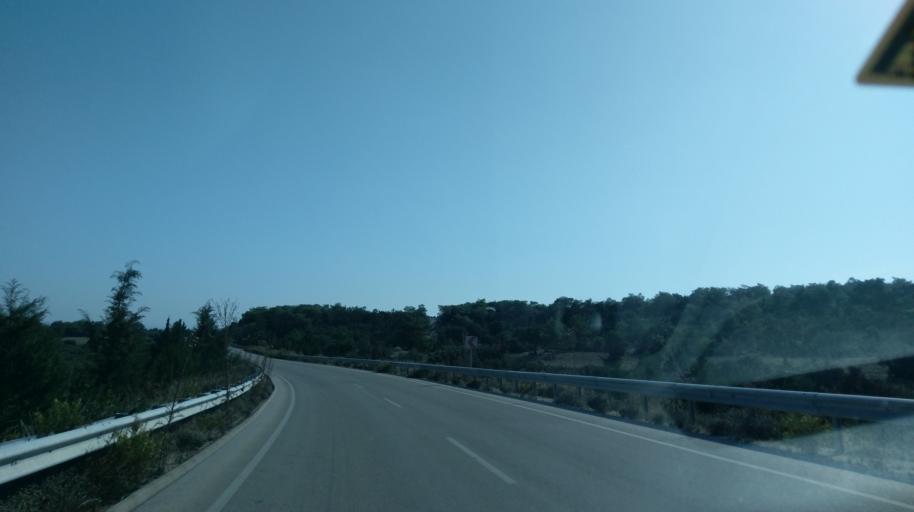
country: CY
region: Ammochostos
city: Trikomo
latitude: 35.4190
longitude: 33.9808
